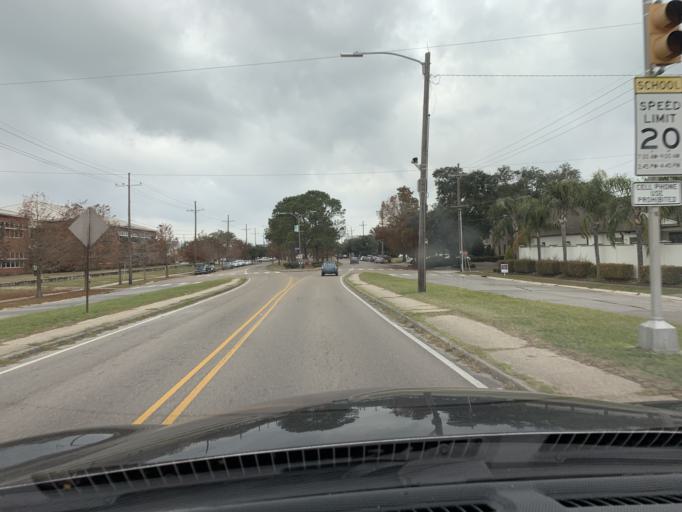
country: US
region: Louisiana
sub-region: Orleans Parish
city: New Orleans
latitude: 30.0041
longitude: -90.1008
